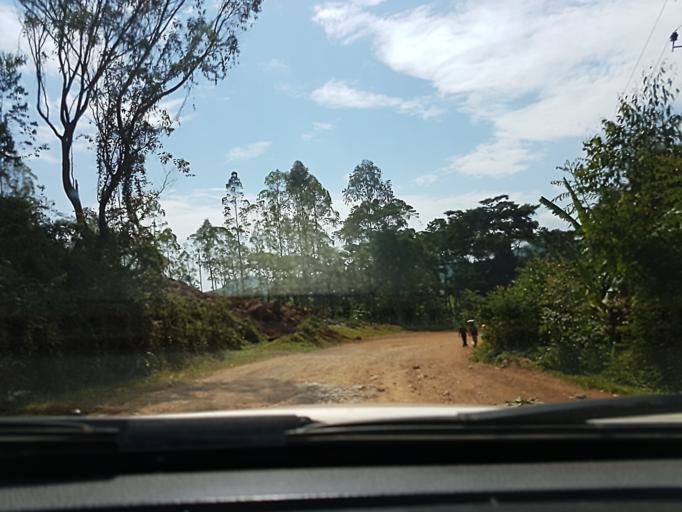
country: CD
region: South Kivu
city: Bukavu
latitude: -2.6532
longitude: 28.8735
